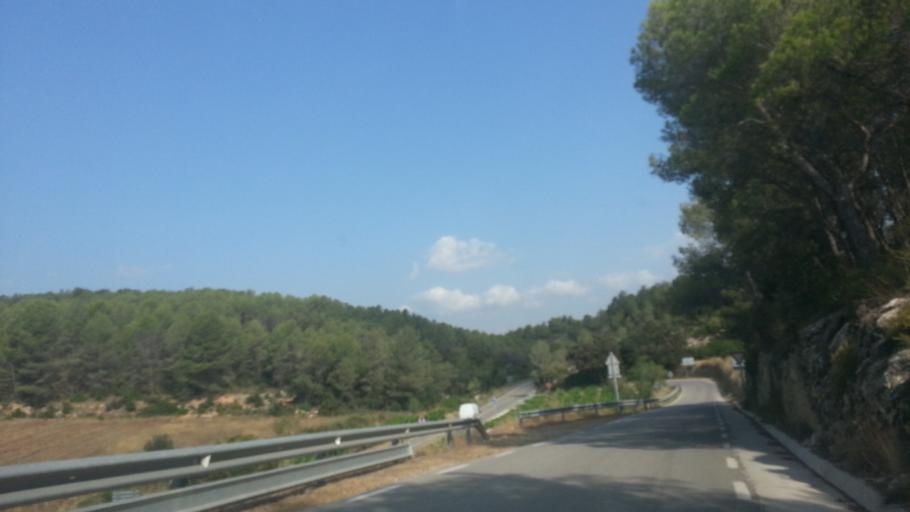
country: ES
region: Catalonia
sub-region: Provincia de Barcelona
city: Avinyonet del Penedes
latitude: 41.3316
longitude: 1.7564
